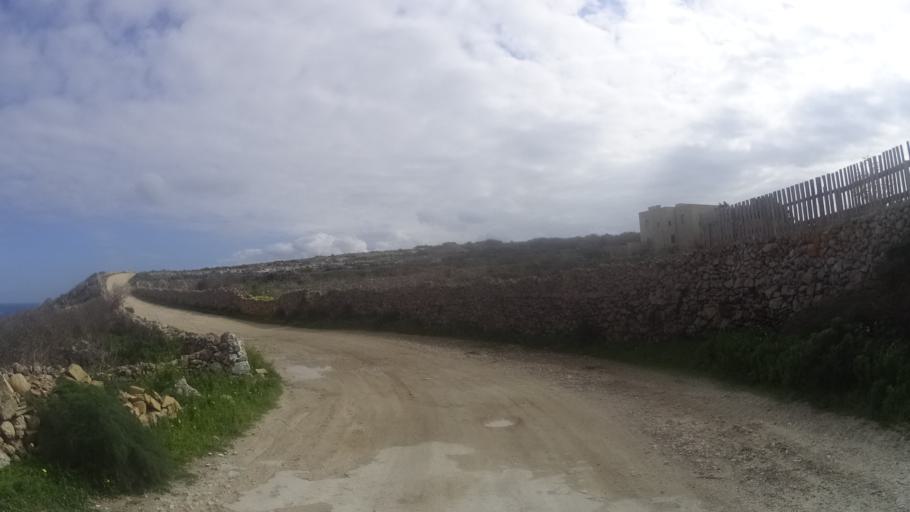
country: MT
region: Il-Qala
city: Qala
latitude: 36.0413
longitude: 14.3183
